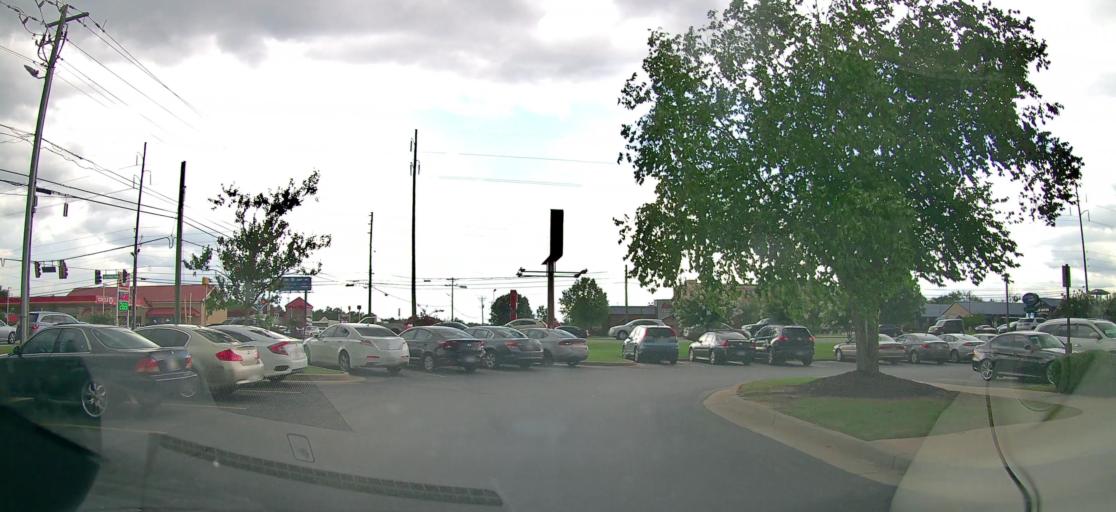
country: US
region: Georgia
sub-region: Houston County
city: Centerville
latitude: 32.6188
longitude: -83.6696
